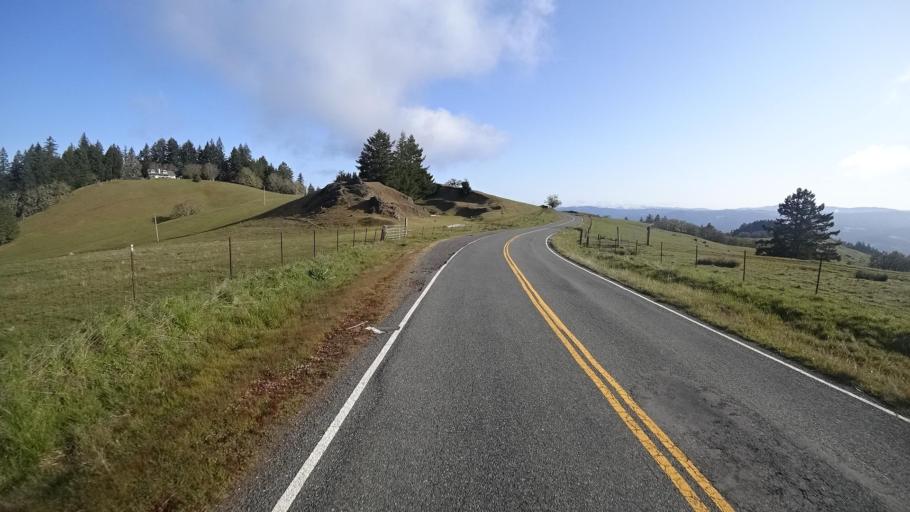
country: US
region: California
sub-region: Humboldt County
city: Blue Lake
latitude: 40.7323
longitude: -123.9476
